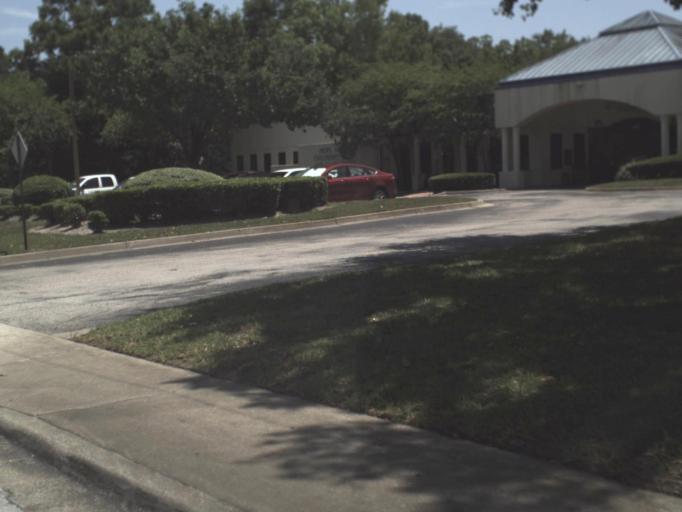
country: US
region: Florida
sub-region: Duval County
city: Jacksonville
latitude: 30.2984
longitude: -81.6195
